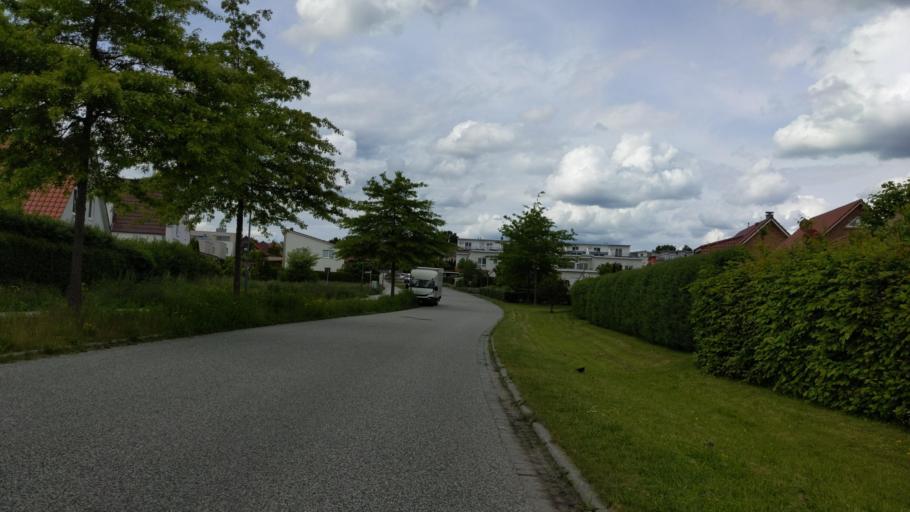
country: DE
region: Schleswig-Holstein
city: Luebeck
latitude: 53.8261
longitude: 10.6829
